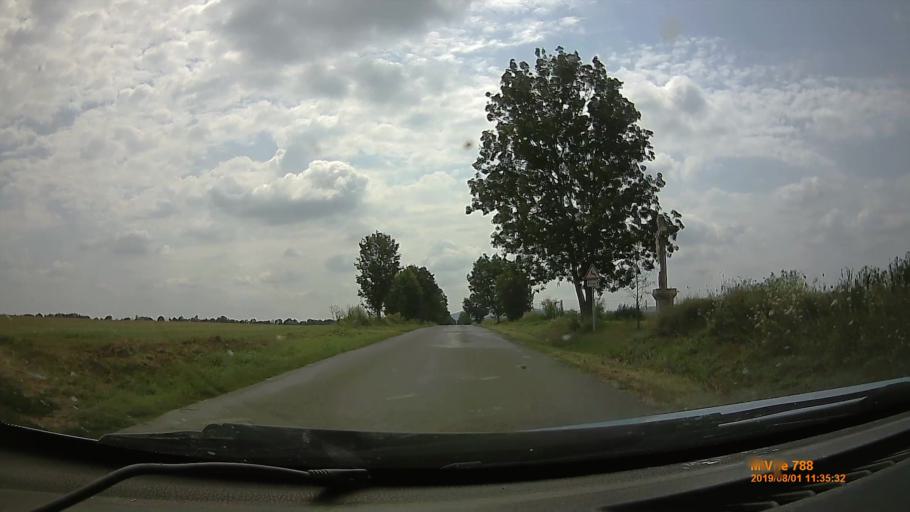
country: HU
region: Baranya
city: Siklos
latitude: 45.9263
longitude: 18.3687
